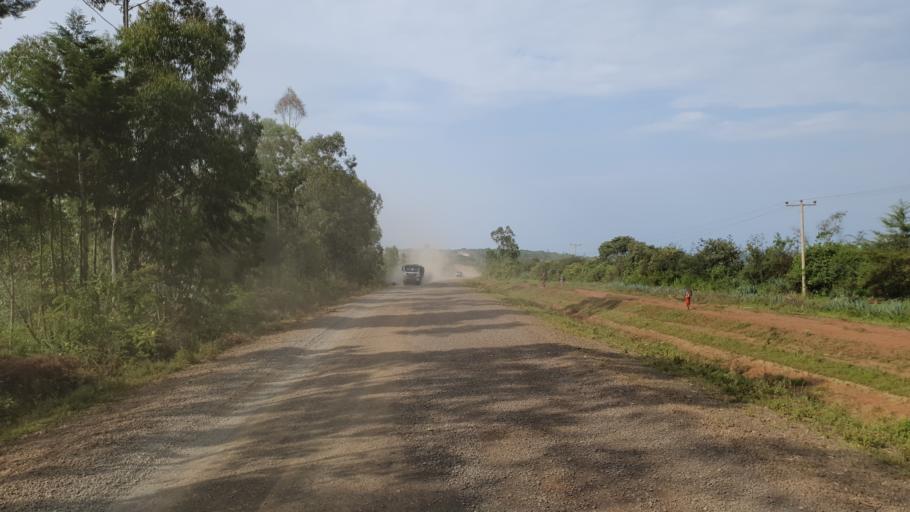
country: ET
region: Oromiya
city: Shambu
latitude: 9.2259
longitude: 36.5167
